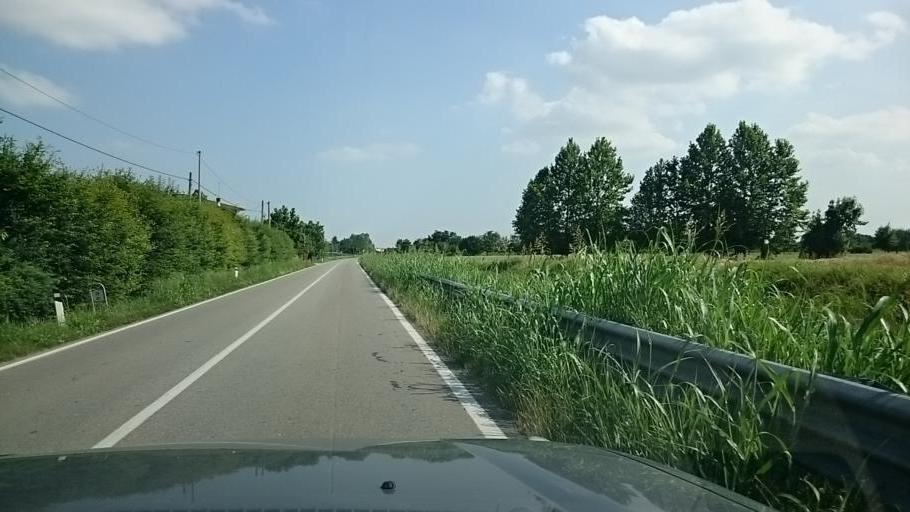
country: IT
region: Veneto
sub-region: Provincia di Padova
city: San Giorgio delle Pertiche
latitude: 45.5533
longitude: 11.8720
